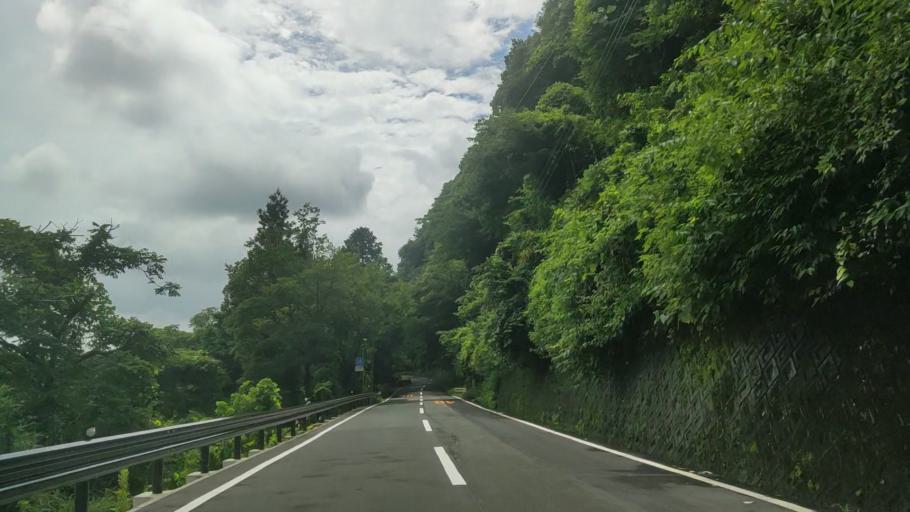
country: JP
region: Shizuoka
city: Fujinomiya
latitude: 35.2089
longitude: 138.5434
